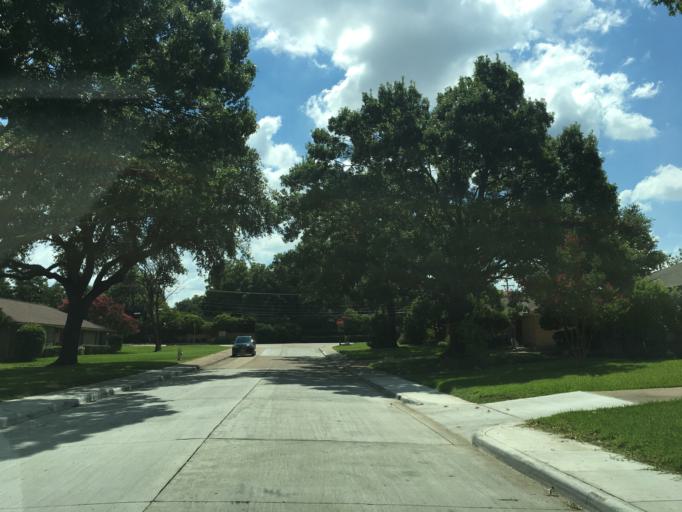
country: US
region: Texas
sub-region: Dallas County
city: Farmers Branch
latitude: 32.9209
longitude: -96.8569
